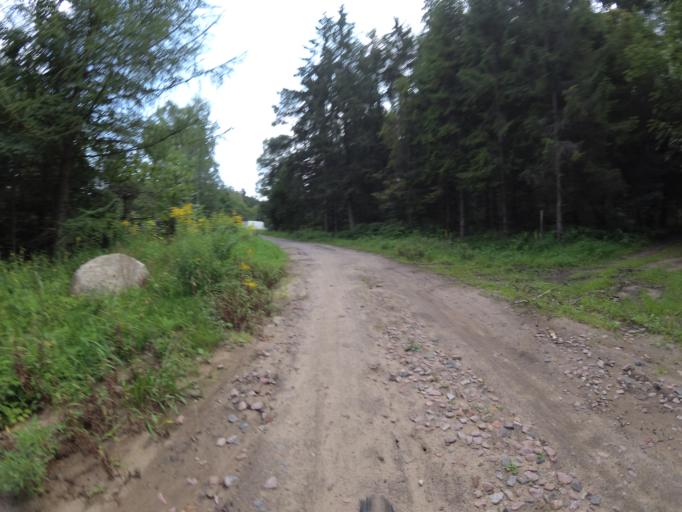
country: PL
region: Pomeranian Voivodeship
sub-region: Gdynia
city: Wielki Kack
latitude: 54.4904
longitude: 18.4631
